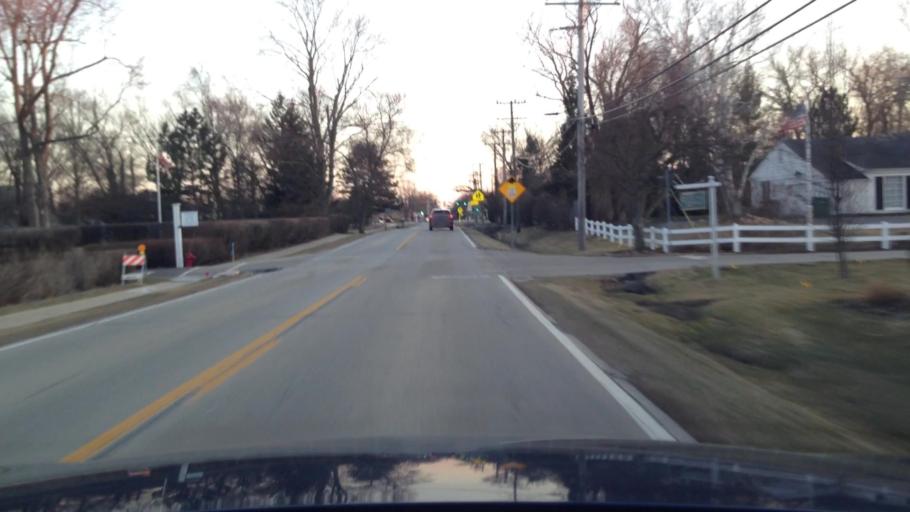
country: US
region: Illinois
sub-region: Cook County
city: Northfield
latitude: 42.1088
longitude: -87.7902
